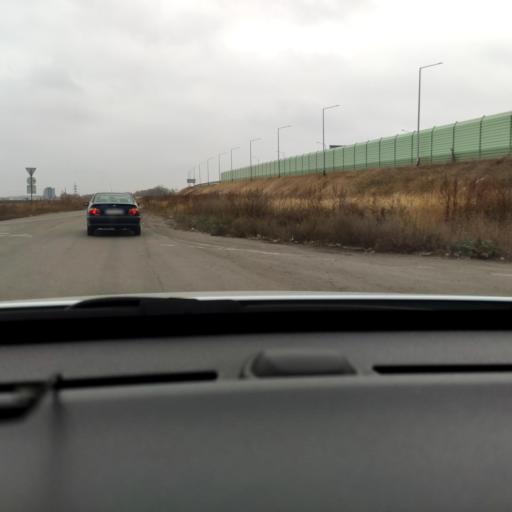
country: RU
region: Voronezj
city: Novaya Usman'
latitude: 51.6466
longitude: 39.3126
